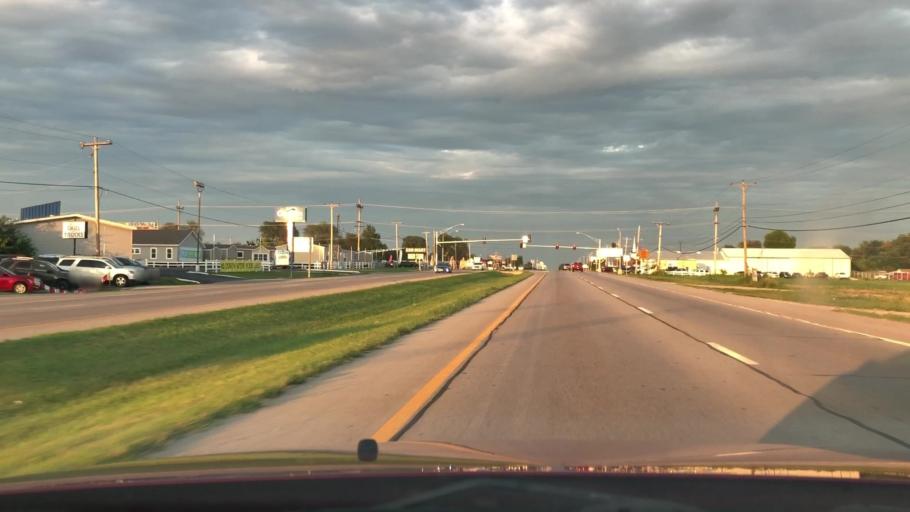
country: US
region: Missouri
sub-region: Greene County
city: Springfield
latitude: 37.1829
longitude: -93.3475
